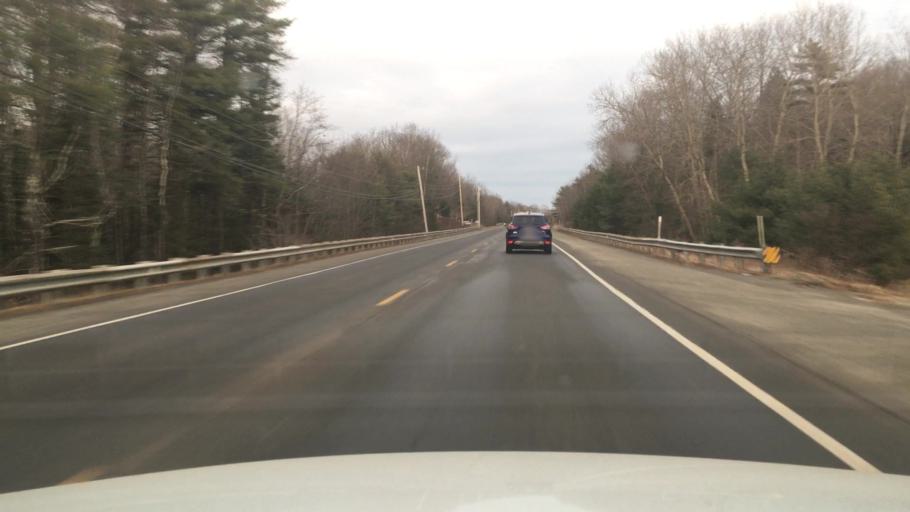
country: US
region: Maine
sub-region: Lincoln County
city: Edgecomb
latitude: 44.0062
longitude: -69.6080
